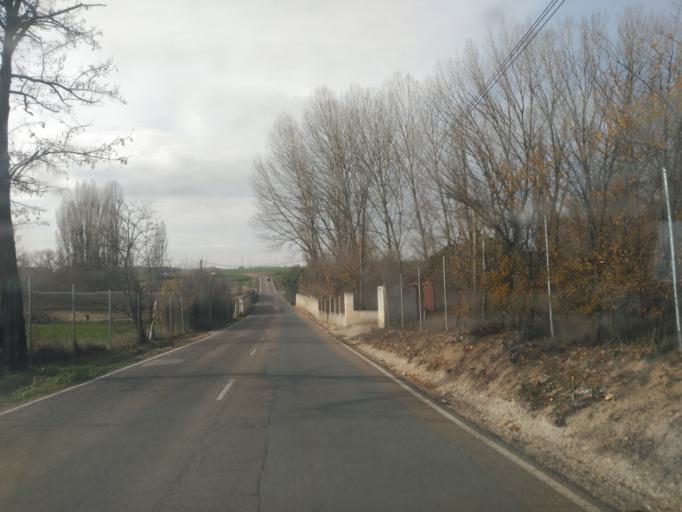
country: ES
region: Castille and Leon
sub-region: Provincia de Salamanca
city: Cabrerizos
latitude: 40.9765
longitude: -5.6212
